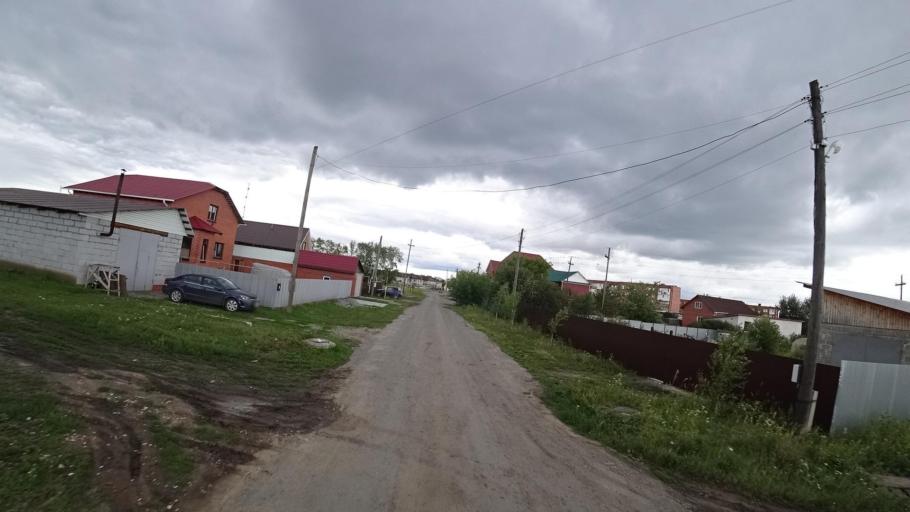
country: RU
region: Sverdlovsk
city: Kamyshlov
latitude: 56.8484
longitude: 62.7414
